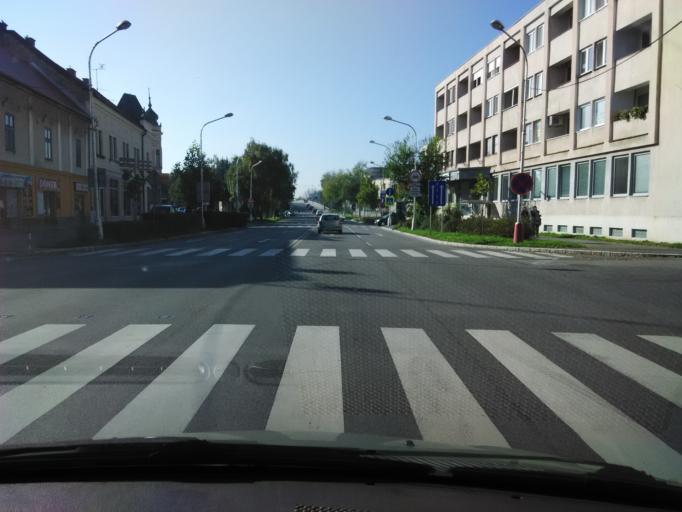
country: SK
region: Nitriansky
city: Komarno
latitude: 47.7594
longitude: 18.1254
